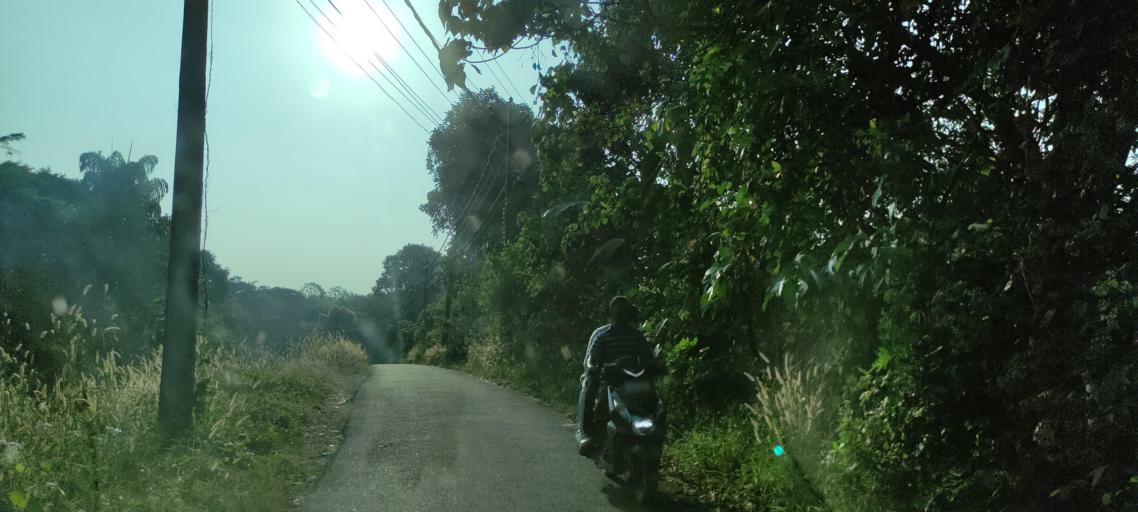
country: IN
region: Kerala
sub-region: Pattanamtitta
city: Adur
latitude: 9.1442
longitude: 76.7348
